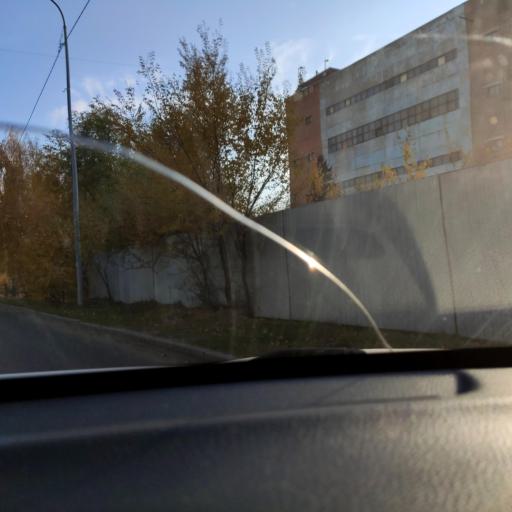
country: RU
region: Tatarstan
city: Staroye Arakchino
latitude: 55.8362
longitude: 49.0372
